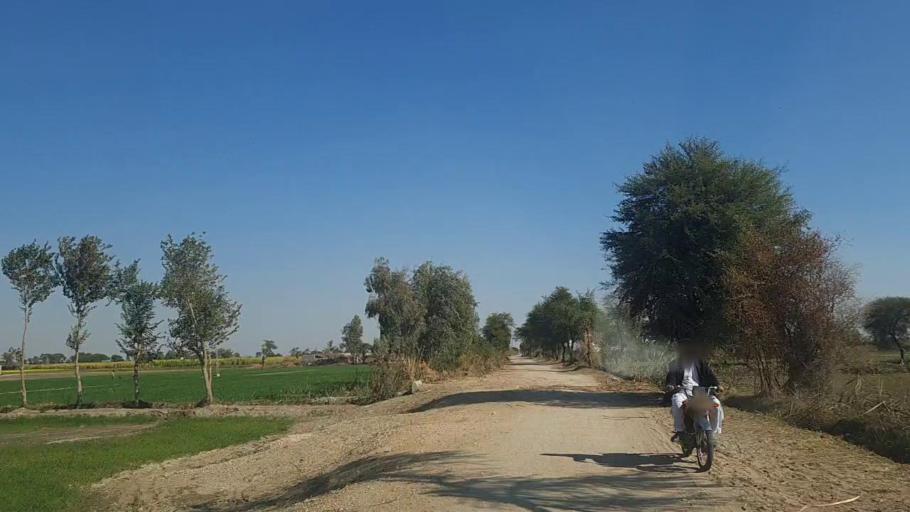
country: PK
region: Sindh
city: Sanghar
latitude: 26.2207
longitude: 68.9294
